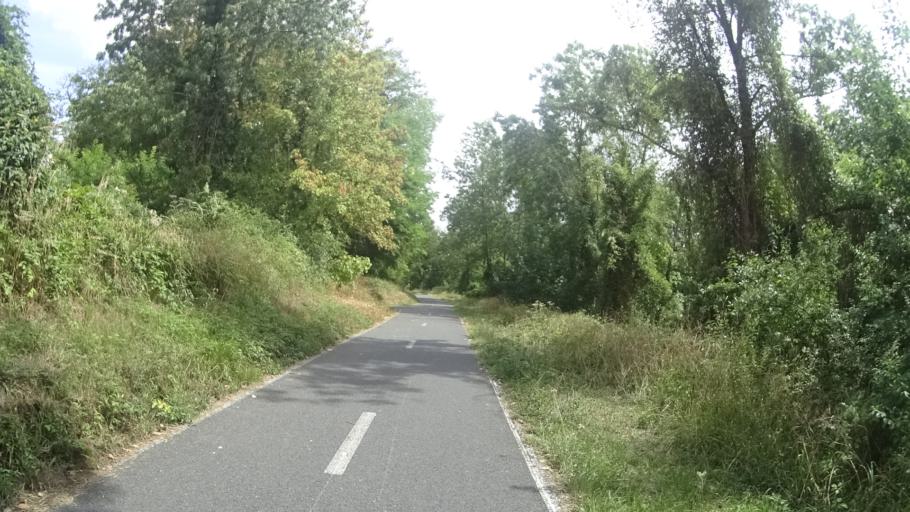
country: FR
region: Ile-de-France
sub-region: Departement de Seine-et-Marne
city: Villeparisis
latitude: 48.9511
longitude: 2.6107
